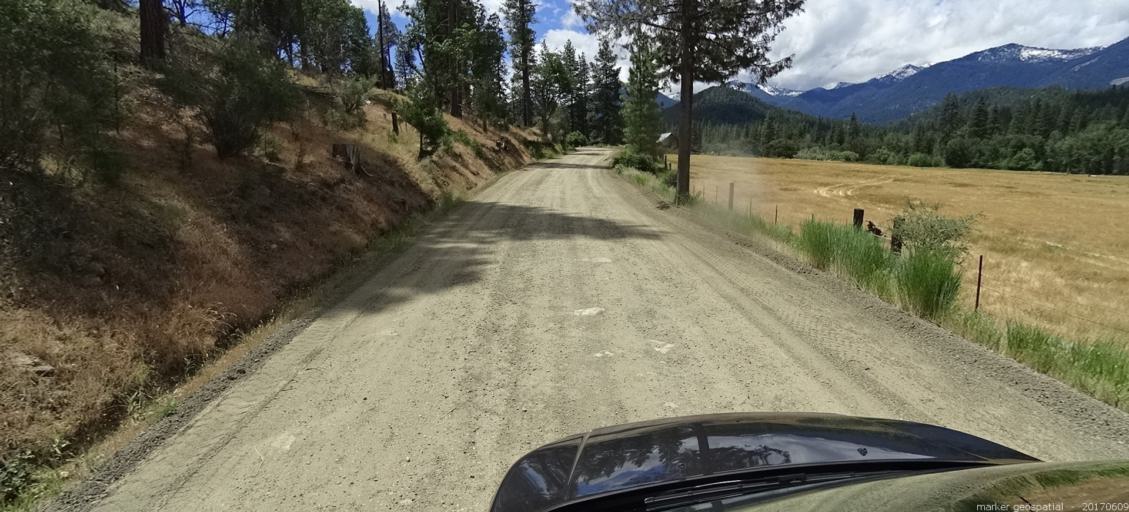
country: US
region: California
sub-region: Siskiyou County
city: Yreka
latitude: 41.3904
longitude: -122.8670
